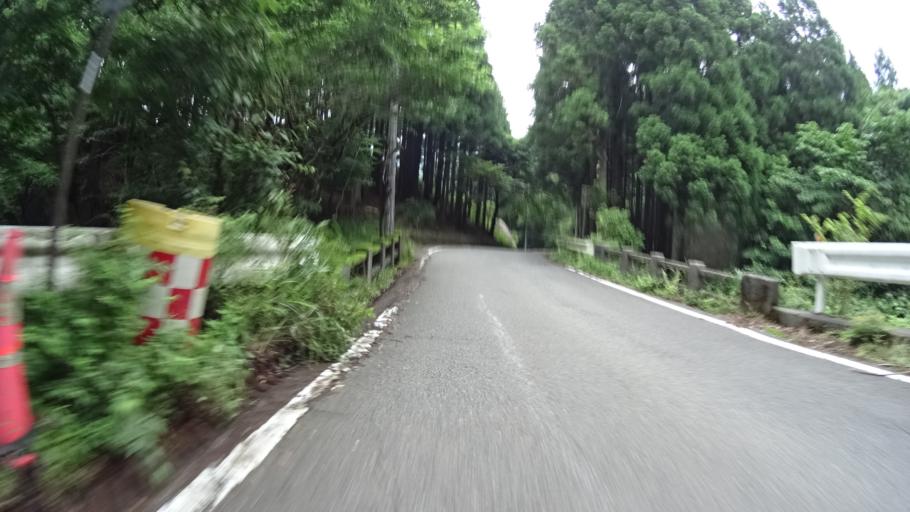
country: JP
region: Kanagawa
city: Hadano
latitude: 35.4319
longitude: 139.2096
